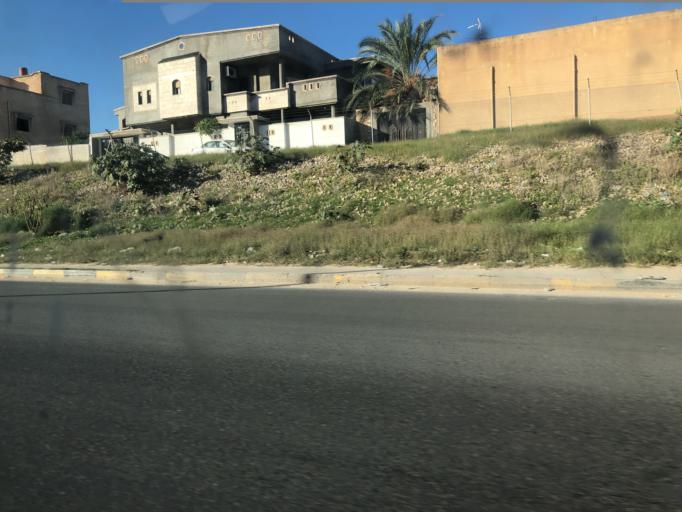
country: LY
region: Tripoli
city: Tripoli
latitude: 32.8689
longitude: 13.2442
